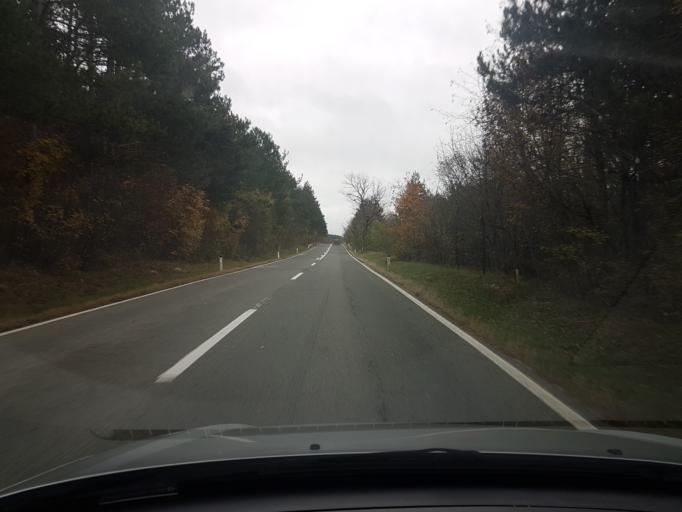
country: SI
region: Divaca
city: Divaca
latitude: 45.7368
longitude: 13.9475
